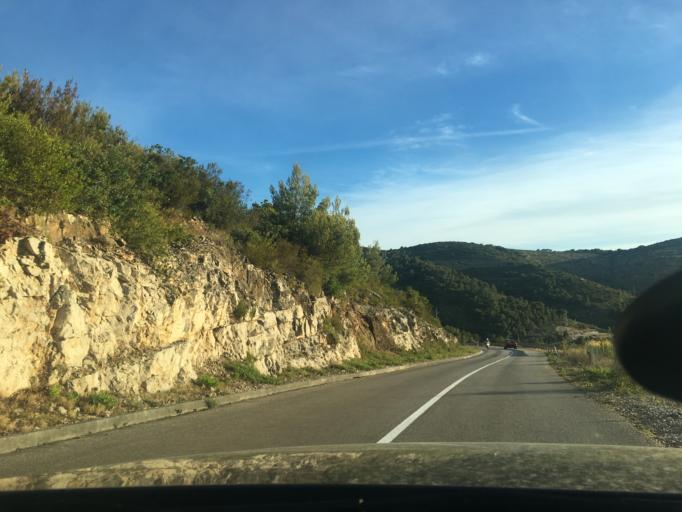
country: HR
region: Splitsko-Dalmatinska
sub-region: Grad Vis
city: Vis
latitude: 43.0585
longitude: 16.2061
